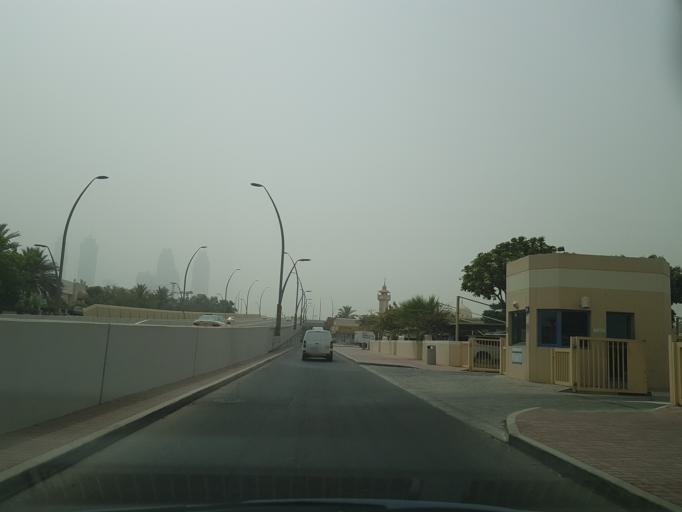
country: AE
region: Dubai
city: Dubai
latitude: 25.1899
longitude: 55.2387
